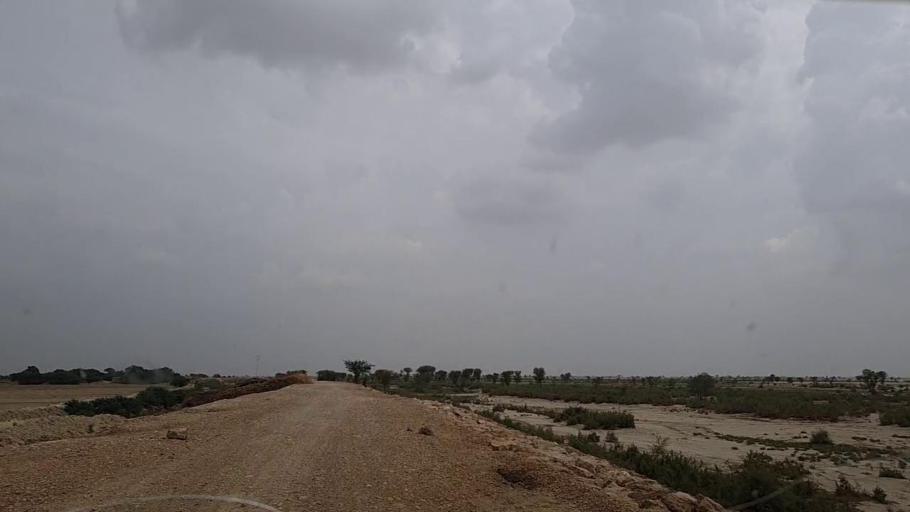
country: PK
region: Sindh
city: Johi
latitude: 26.7257
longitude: 67.5780
